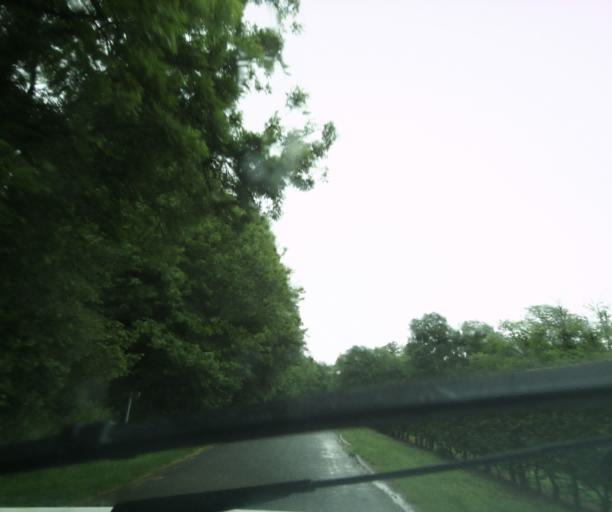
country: FR
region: Bourgogne
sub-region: Departement de Saone-et-Loire
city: Ciry-le-Noble
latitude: 46.5397
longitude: 4.3018
